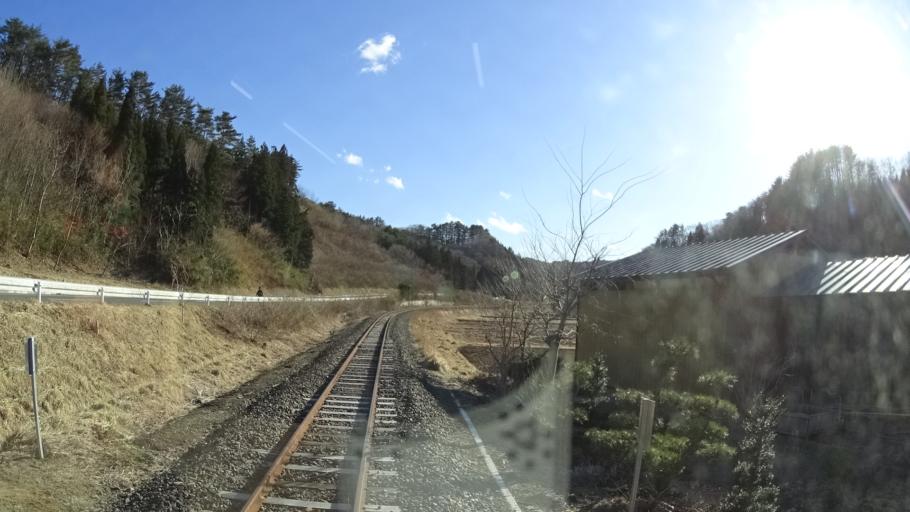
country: JP
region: Iwate
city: Miyako
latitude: 39.6131
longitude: 141.9383
